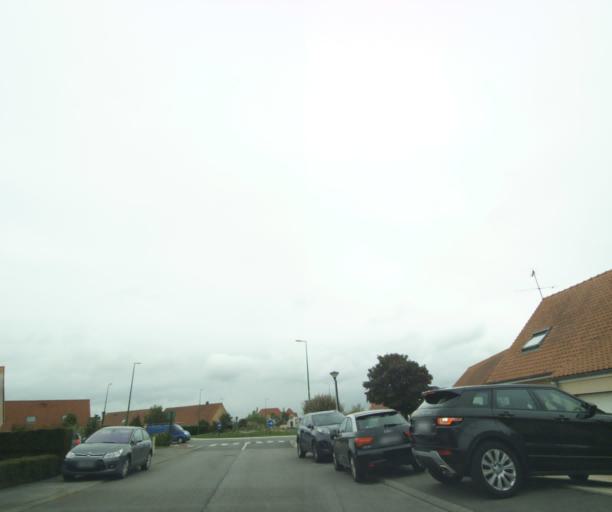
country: FR
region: Nord-Pas-de-Calais
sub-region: Departement du Pas-de-Calais
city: Etaples
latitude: 50.5157
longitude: 1.6537
